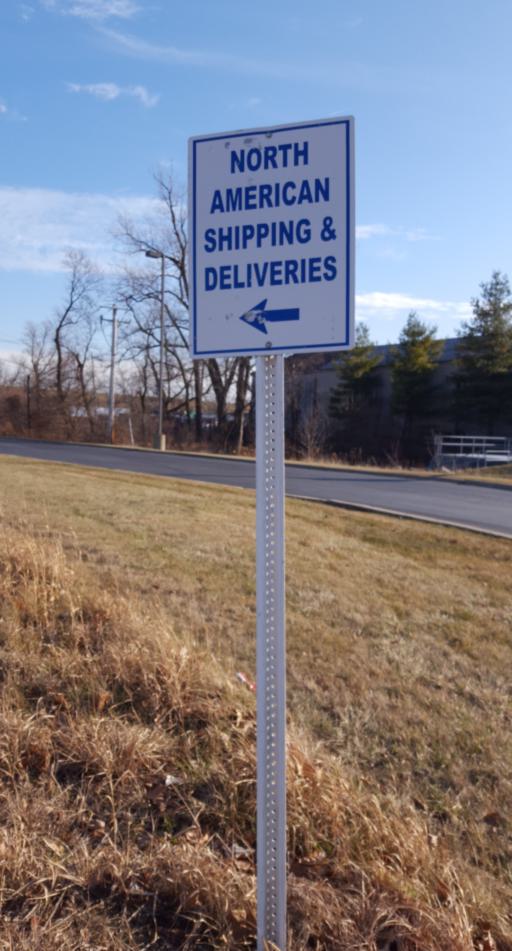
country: US
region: Illinois
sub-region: Cook County
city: Northfield
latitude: 42.0950
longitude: -87.8142
